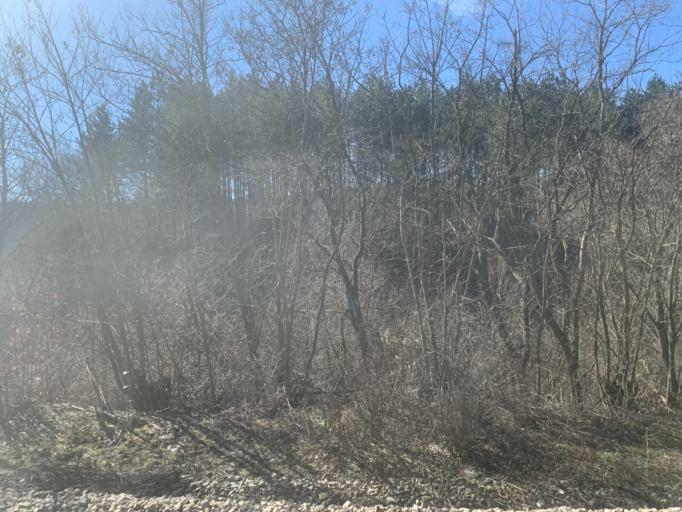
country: BG
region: Sofiya
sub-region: Obshtina Gorna Malina
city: Gorna Malina
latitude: 42.5643
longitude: 23.6851
